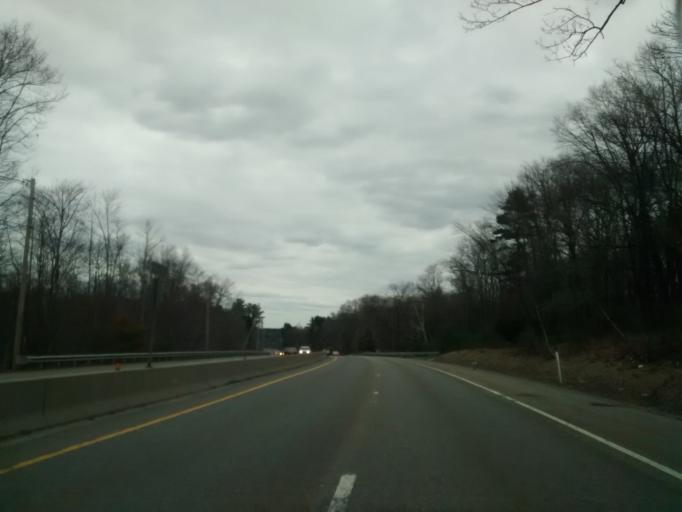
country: US
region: Massachusetts
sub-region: Worcester County
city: Charlton
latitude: 42.1470
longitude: -71.9358
